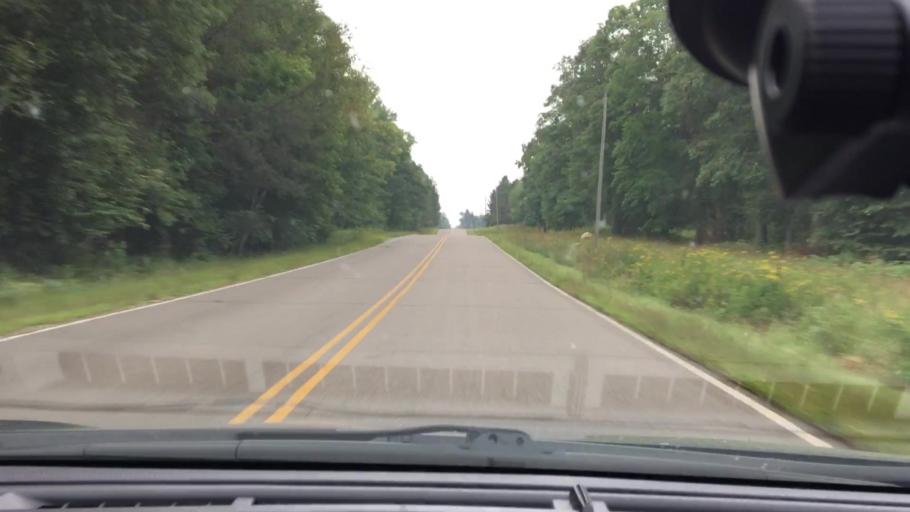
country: US
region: Minnesota
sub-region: Crow Wing County
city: Cross Lake
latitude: 46.6512
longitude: -94.0095
